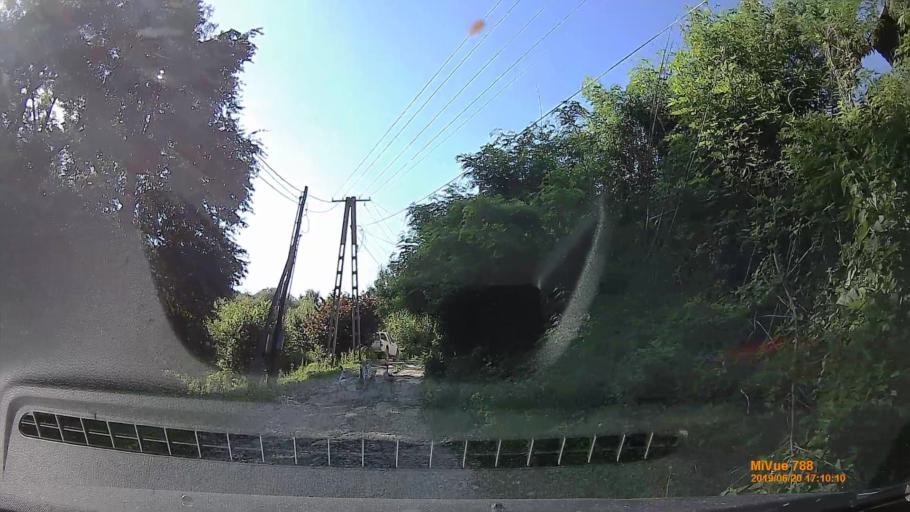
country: HU
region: Baranya
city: Buekkoesd
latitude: 46.1437
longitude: 18.0052
